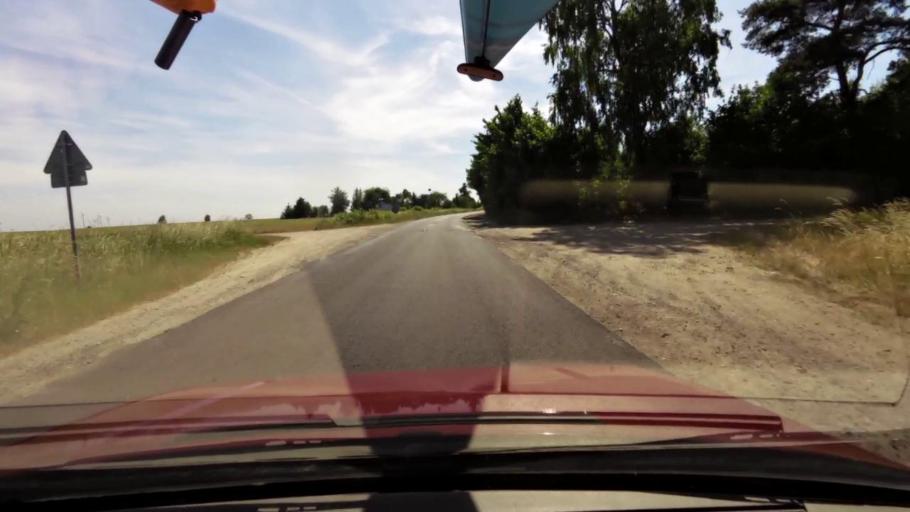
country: PL
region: Pomeranian Voivodeship
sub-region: Powiat slupski
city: Kobylnica
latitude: 54.3978
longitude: 16.9919
